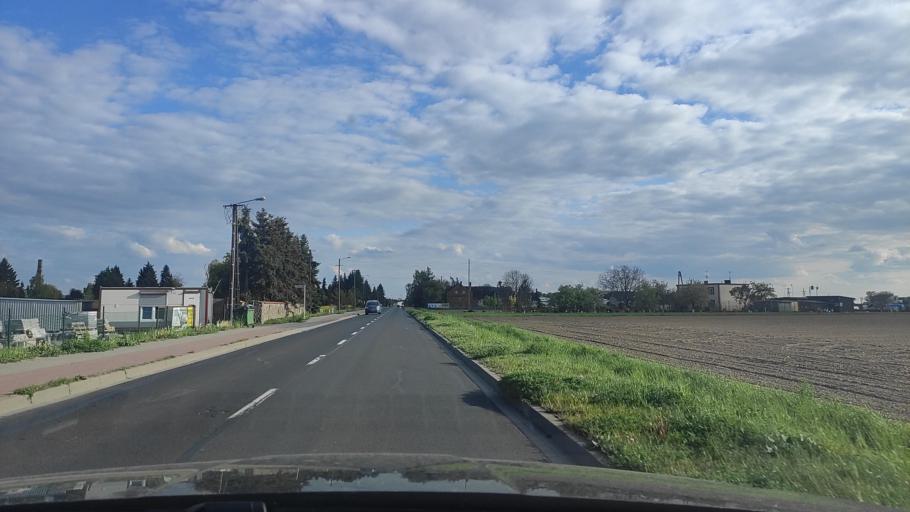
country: PL
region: Greater Poland Voivodeship
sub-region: Powiat poznanski
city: Kostrzyn
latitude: 52.4084
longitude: 17.2252
